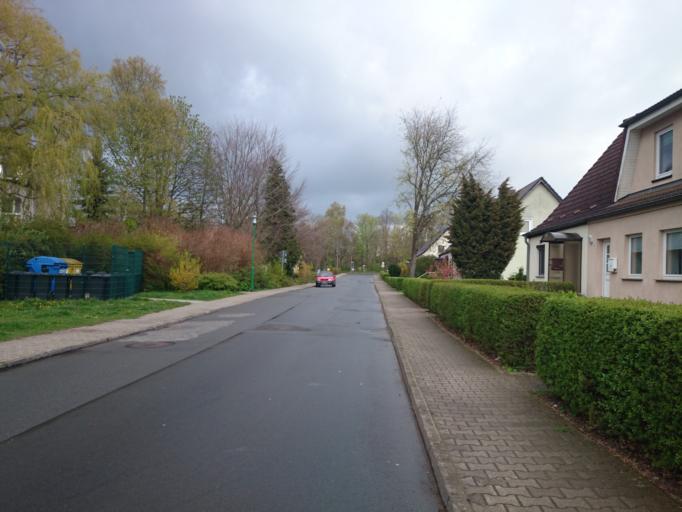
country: DE
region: Mecklenburg-Vorpommern
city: Broderstorf
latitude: 54.0725
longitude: 12.3383
